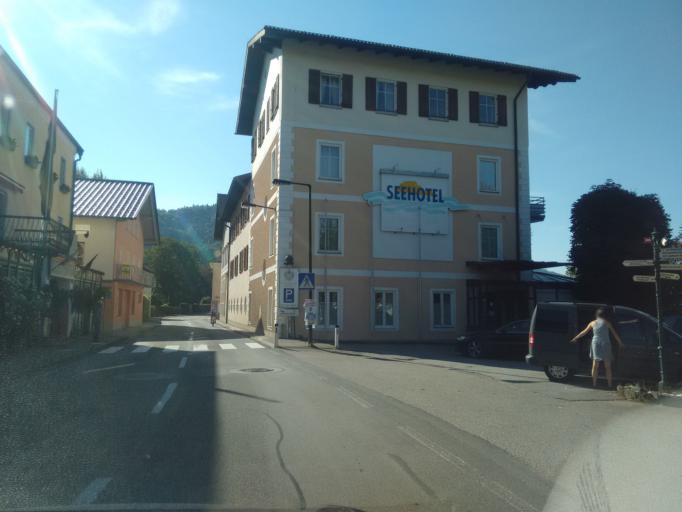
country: AT
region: Upper Austria
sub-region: Politischer Bezirk Vocklabruck
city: Attersee
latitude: 47.9001
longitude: 13.5697
